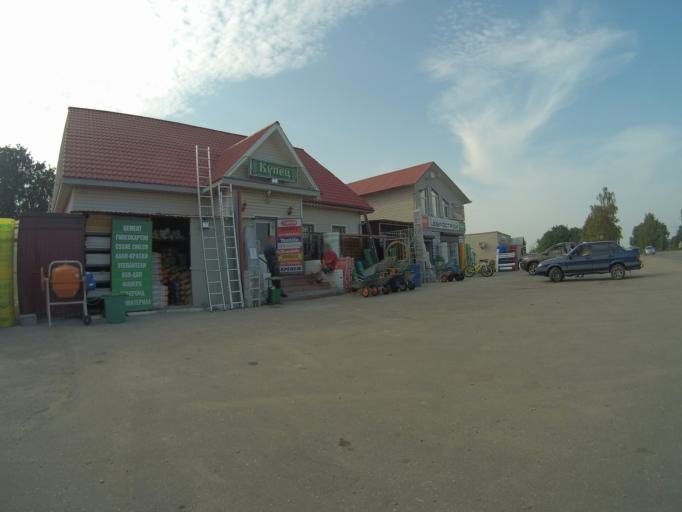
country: RU
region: Vladimir
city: Suzdal'
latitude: 56.4284
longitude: 40.4172
